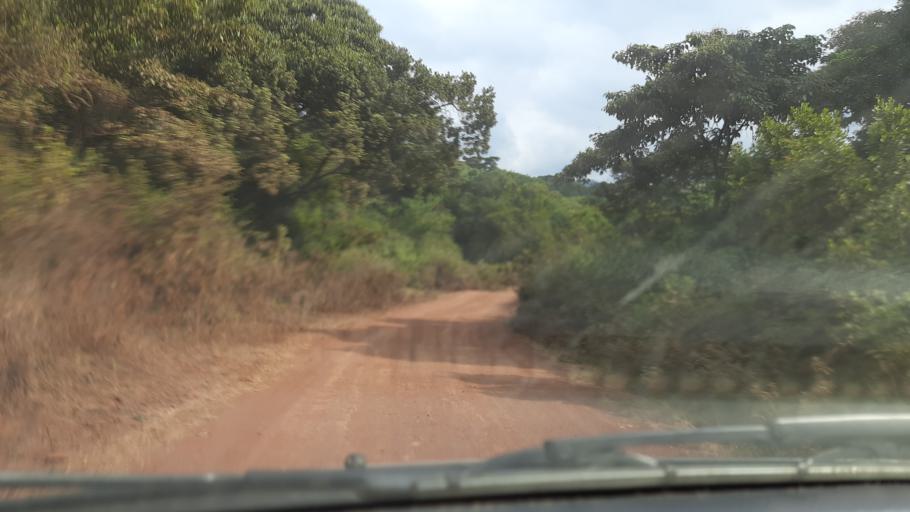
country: TZ
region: Kilimanjaro
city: Moshi
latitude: -2.8601
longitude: 37.2656
